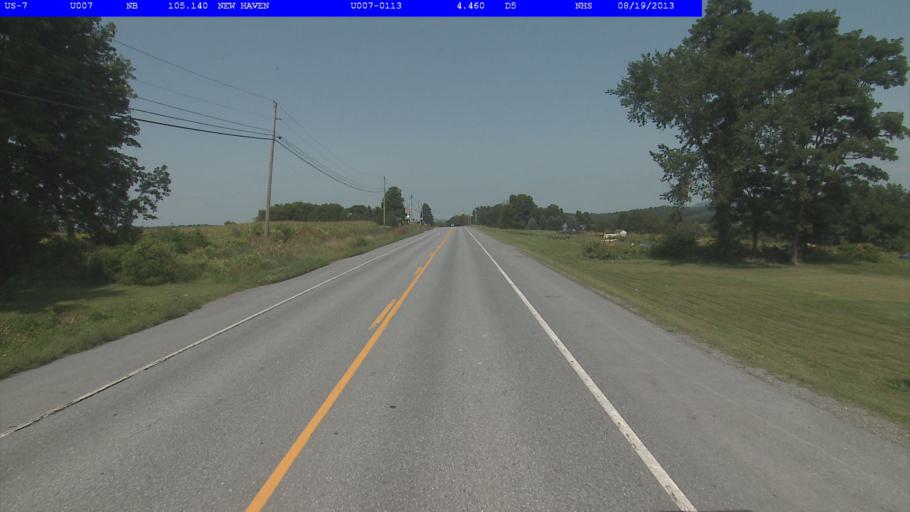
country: US
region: Vermont
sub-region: Addison County
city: Middlebury (village)
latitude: 44.1096
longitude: -73.1747
